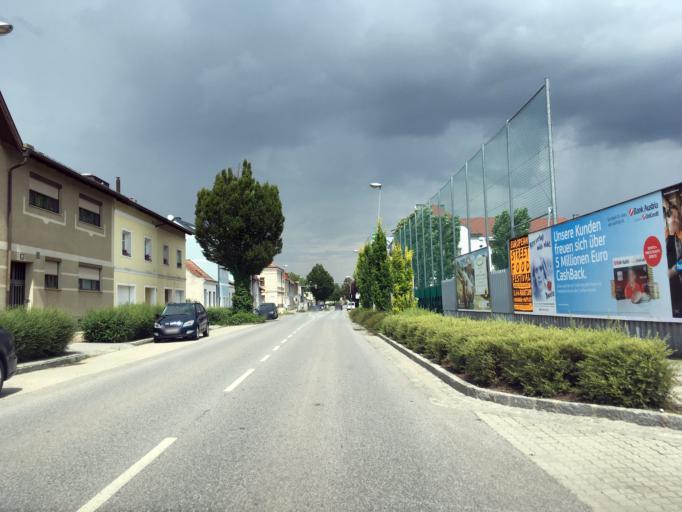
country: AT
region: Lower Austria
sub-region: Politischer Bezirk Korneuburg
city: Korneuburg
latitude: 48.3478
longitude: 16.3360
